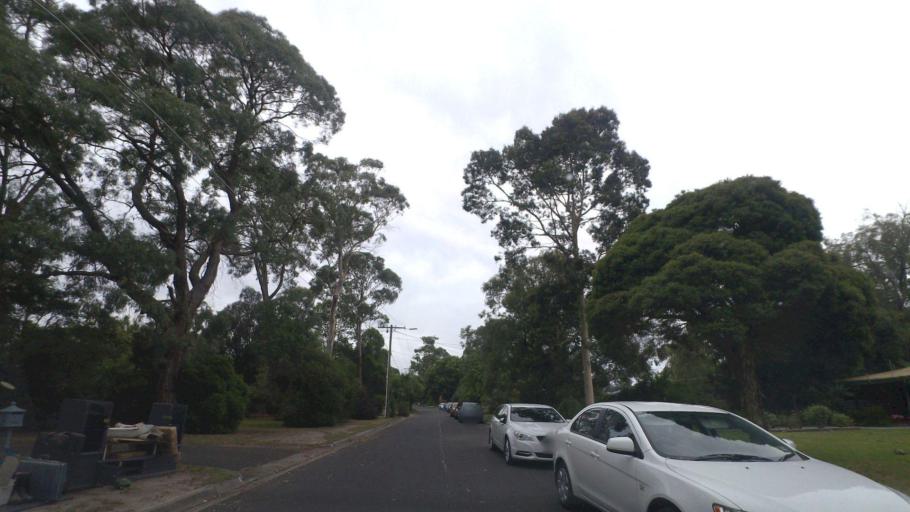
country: AU
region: Victoria
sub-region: Yarra Ranges
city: Kilsyth
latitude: -37.7861
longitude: 145.3337
